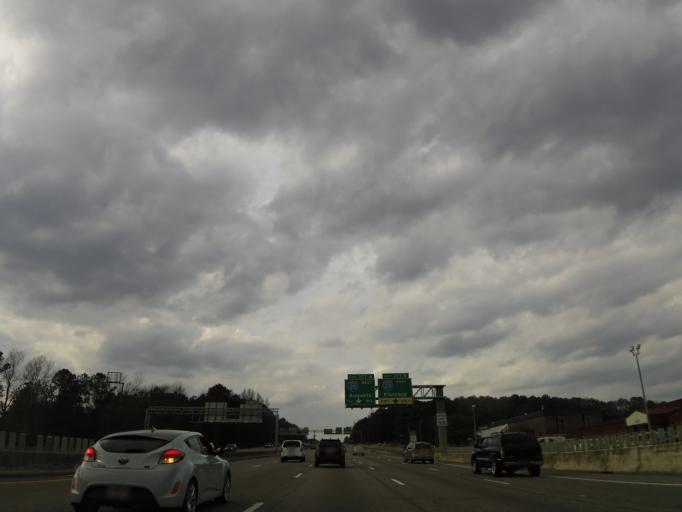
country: US
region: South Carolina
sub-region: Lexington County
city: Saint Andrews
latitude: 34.0317
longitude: -81.1051
